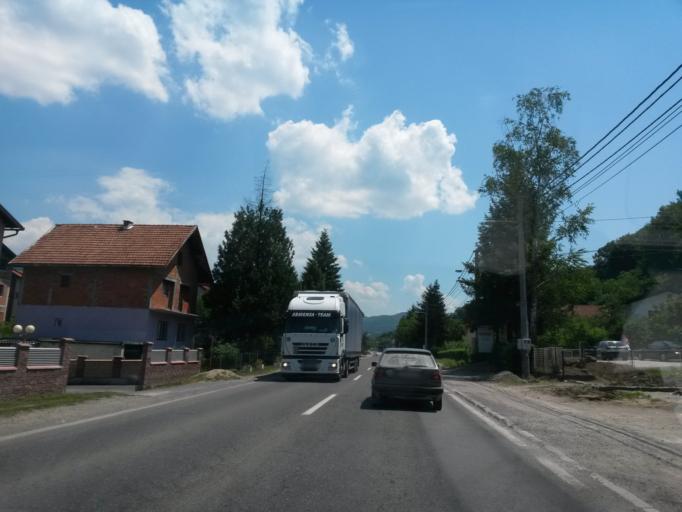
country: BA
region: Republika Srpska
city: Doboj
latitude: 44.7554
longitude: 18.0784
